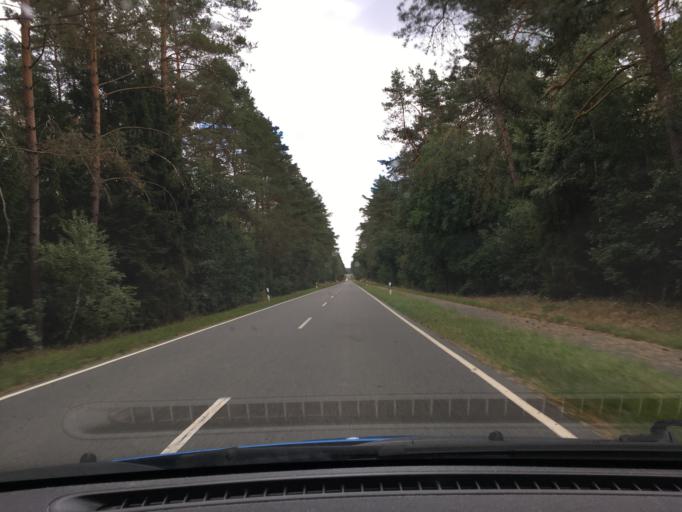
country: DE
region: Lower Saxony
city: Jesteburg
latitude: 53.2570
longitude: 9.9134
